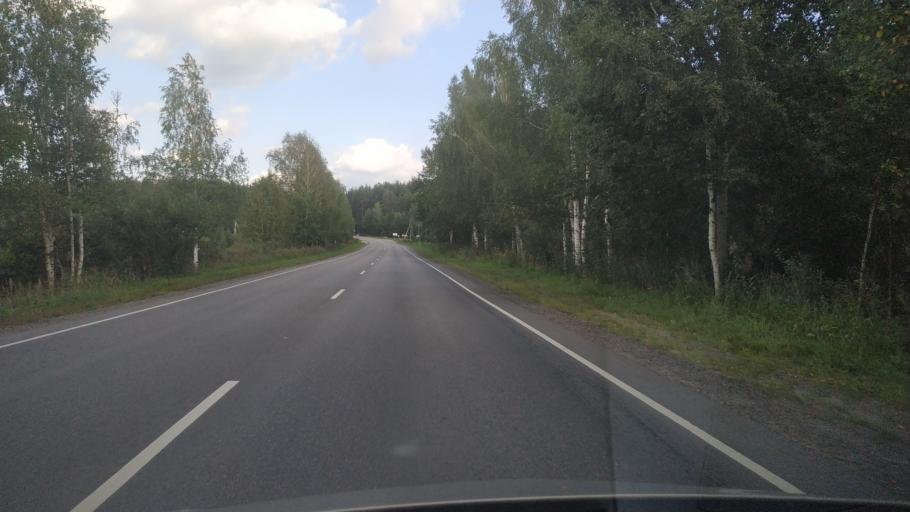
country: RU
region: Moskovskaya
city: Vereya
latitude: 55.7041
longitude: 39.1620
